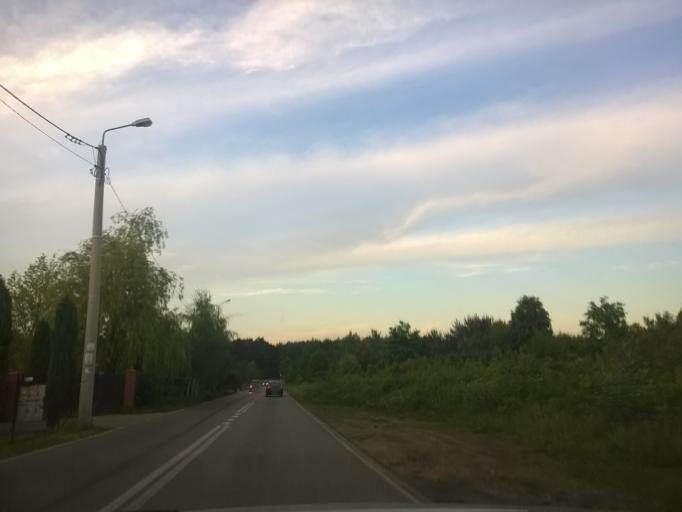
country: PL
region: Masovian Voivodeship
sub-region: Powiat piaseczynski
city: Baniocha
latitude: 52.0023
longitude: 21.1108
